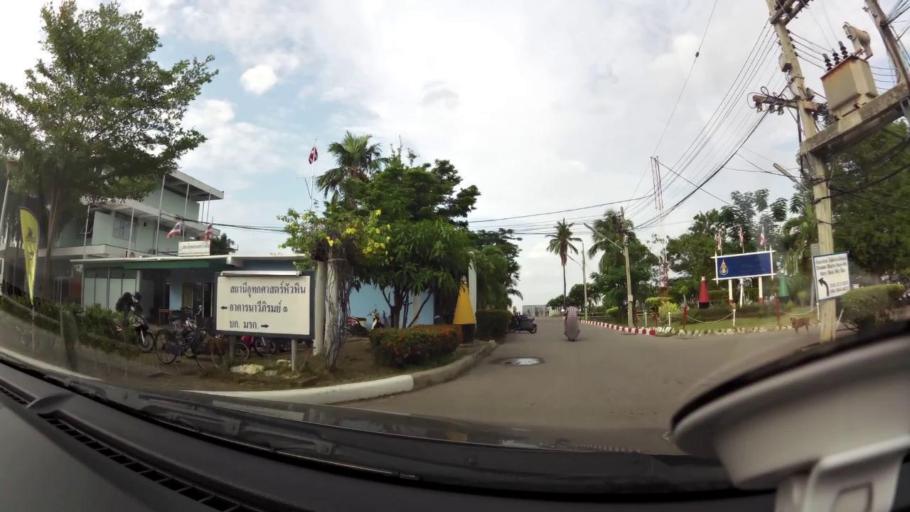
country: TH
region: Prachuap Khiri Khan
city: Hua Hin
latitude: 12.5760
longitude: 99.9573
